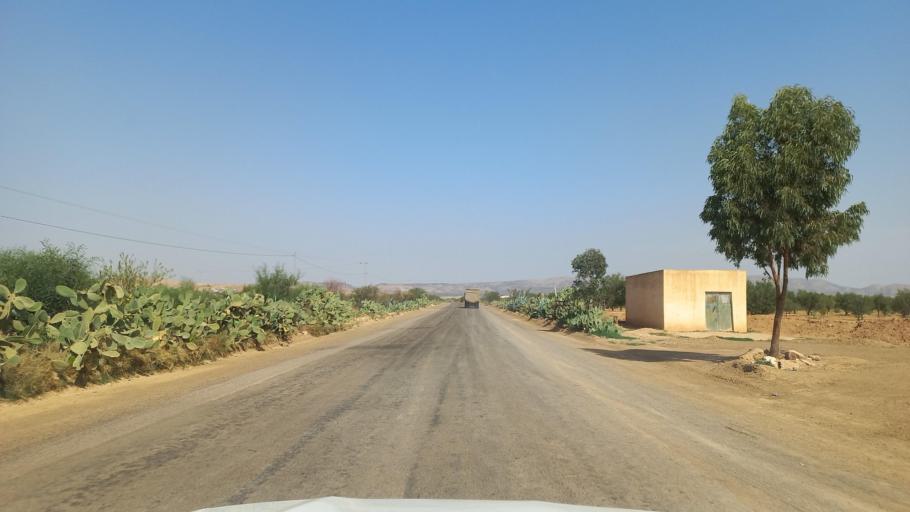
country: TN
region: Al Qasrayn
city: Sbiba
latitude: 35.3541
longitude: 9.0498
